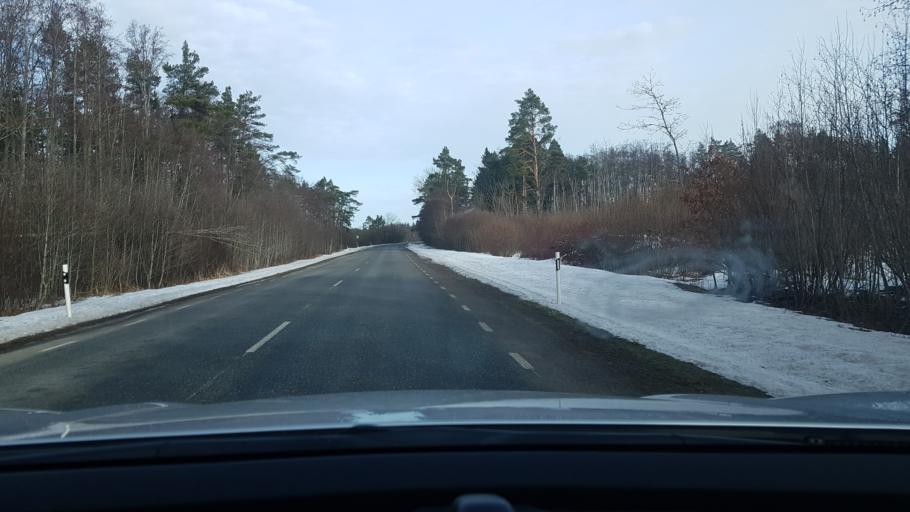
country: EE
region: Saare
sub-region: Kuressaare linn
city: Kuressaare
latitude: 58.4007
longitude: 22.6427
